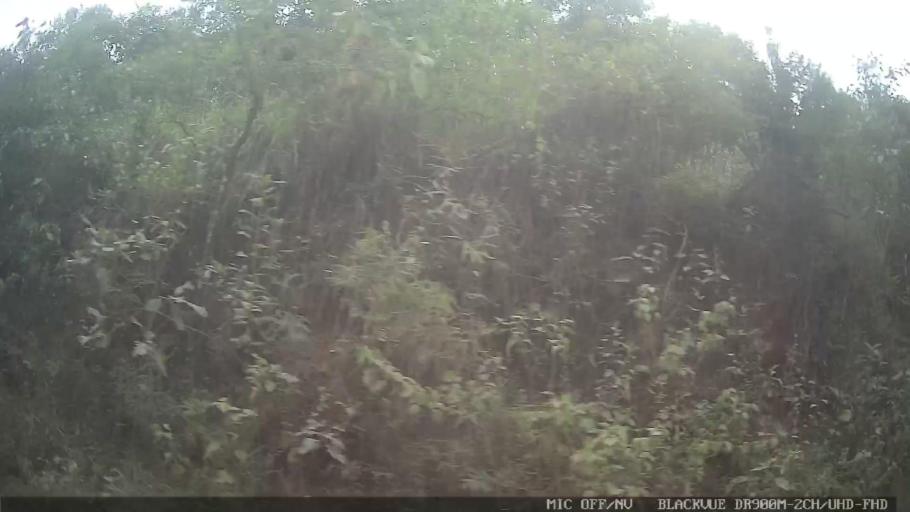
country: BR
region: Sao Paulo
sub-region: Atibaia
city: Atibaia
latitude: -23.1660
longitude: -46.5284
